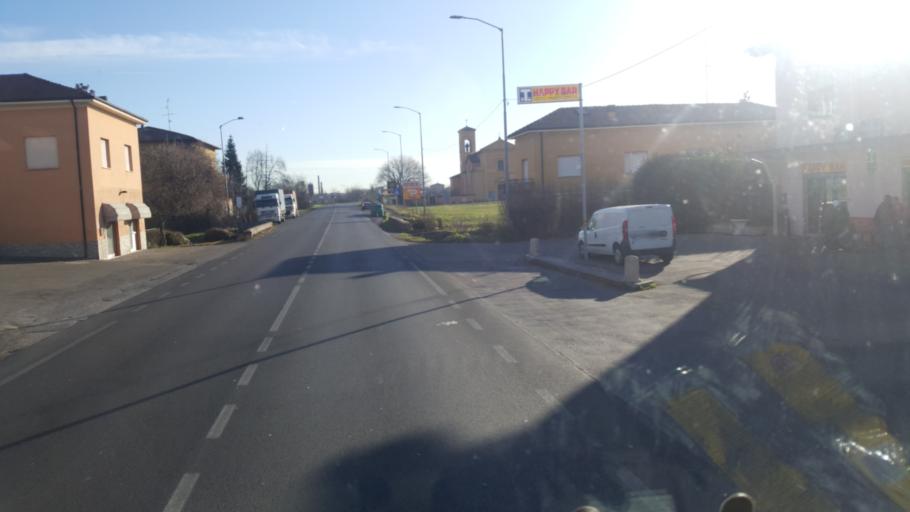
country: IT
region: Emilia-Romagna
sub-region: Provincia di Modena
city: Campogalliano
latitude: 44.6478
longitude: 10.8420
